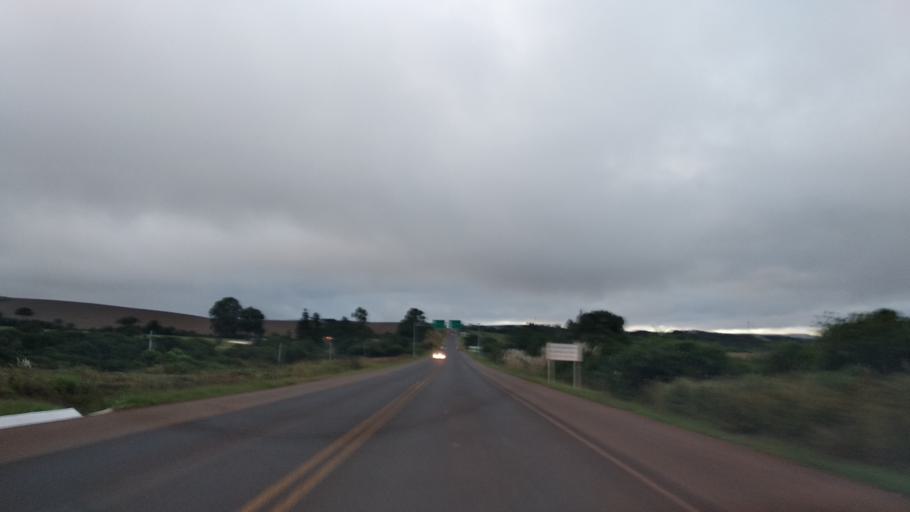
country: BR
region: Santa Catarina
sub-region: Campos Novos
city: Campos Novos
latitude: -27.3766
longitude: -51.0649
